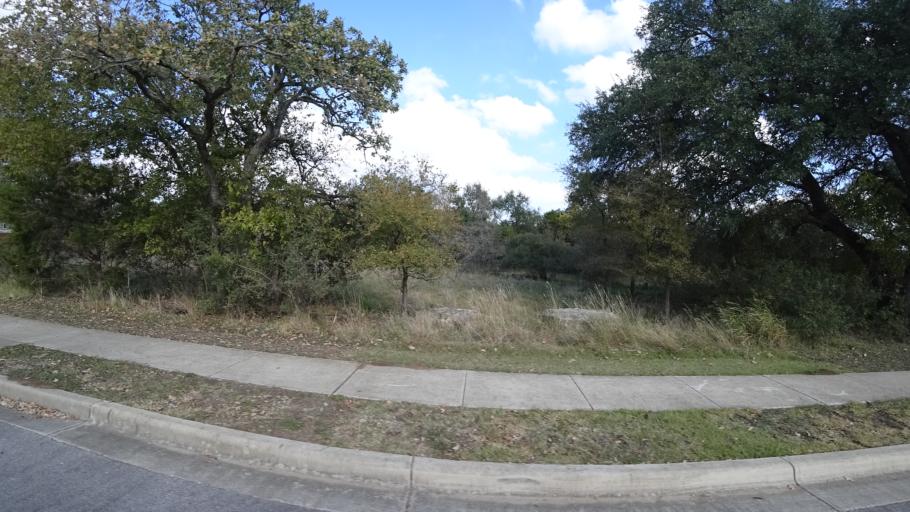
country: US
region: Texas
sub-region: Travis County
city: Shady Hollow
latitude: 30.1619
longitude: -97.8478
